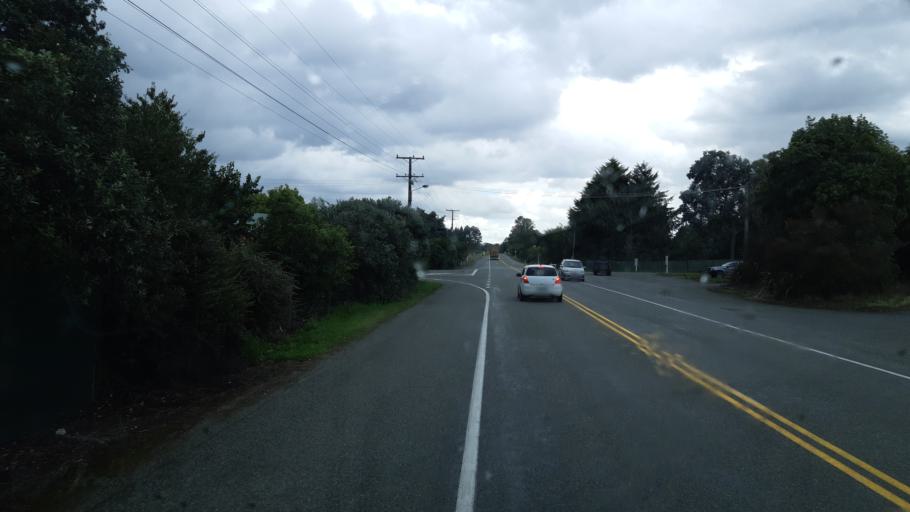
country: NZ
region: Tasman
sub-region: Tasman District
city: Wakefield
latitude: -41.4501
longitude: 172.9586
